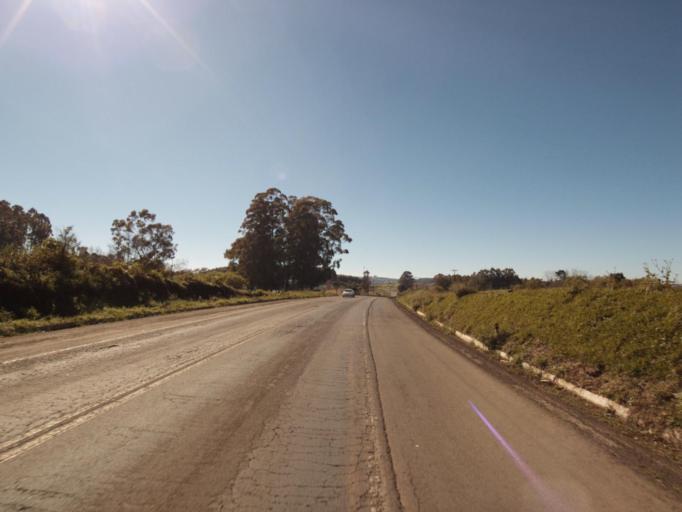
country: BR
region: Rio Grande do Sul
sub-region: Frederico Westphalen
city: Frederico Westphalen
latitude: -26.9194
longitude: -53.1966
